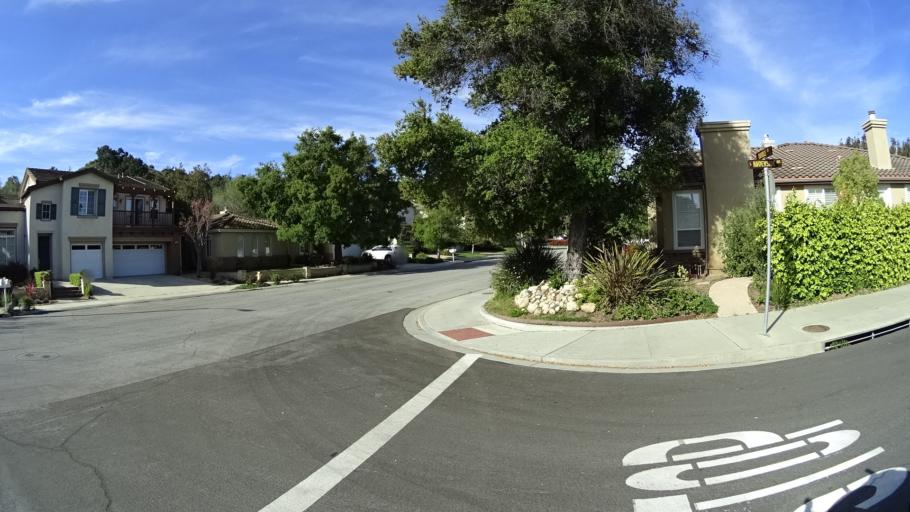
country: US
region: California
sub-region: Ventura County
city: Casa Conejo
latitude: 34.1682
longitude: -118.9594
